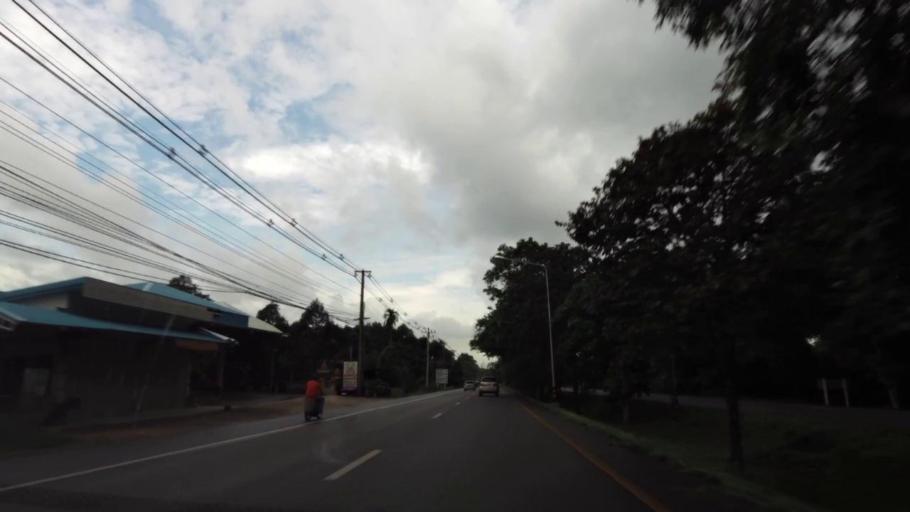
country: TH
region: Chanthaburi
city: Khlung
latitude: 12.4803
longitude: 102.1840
